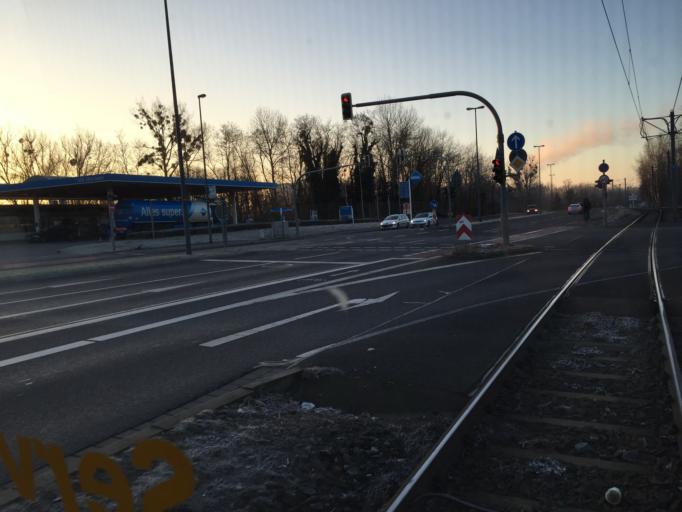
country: DE
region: Saxony
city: Albertstadt
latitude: 51.0943
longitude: 13.7667
